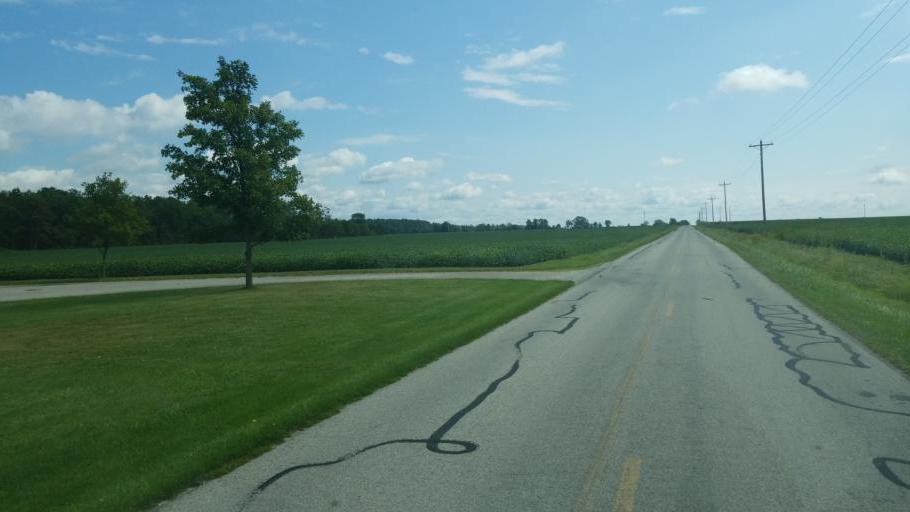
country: US
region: Ohio
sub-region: Seneca County
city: Tiffin
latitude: 41.0666
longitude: -83.0603
